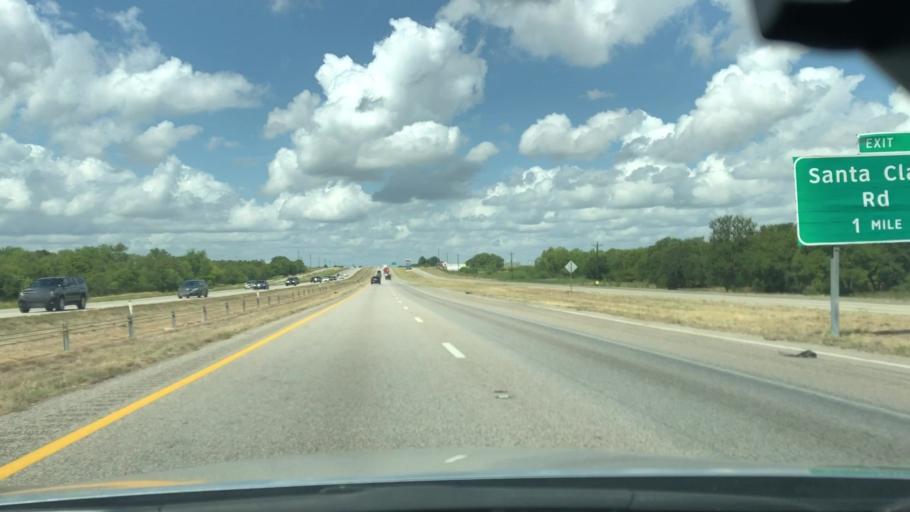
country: US
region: Texas
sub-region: Guadalupe County
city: Marion
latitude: 29.5264
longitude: -98.1195
